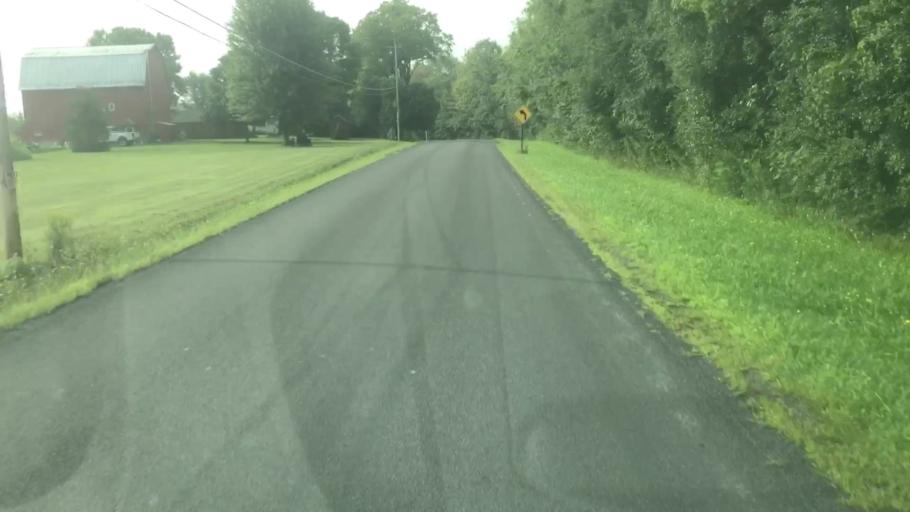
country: US
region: New York
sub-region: Onondaga County
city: Skaneateles
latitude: 42.9144
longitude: -76.4562
